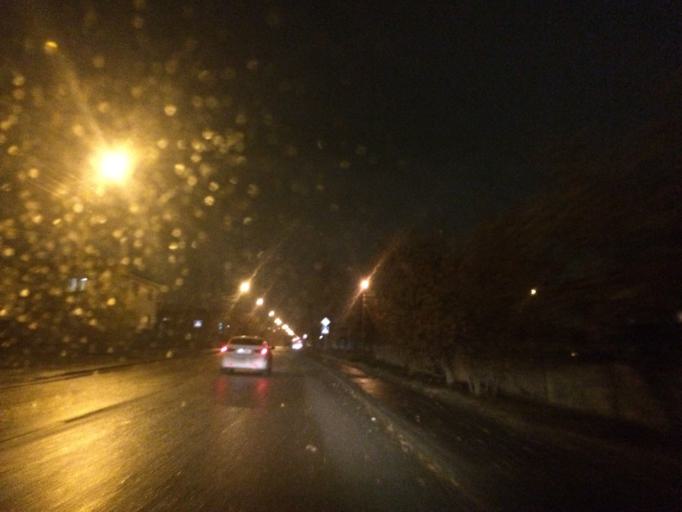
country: KZ
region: Astana Qalasy
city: Astana
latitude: 51.1847
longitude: 71.3812
